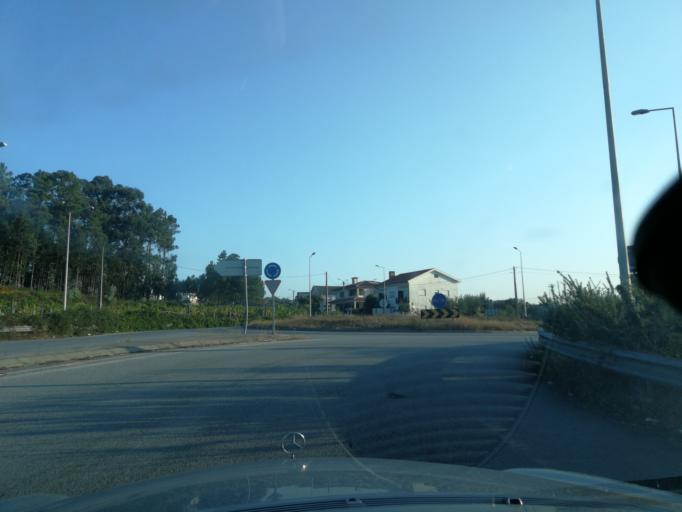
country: PT
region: Braga
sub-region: Braga
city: Braga
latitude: 41.5181
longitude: -8.4286
